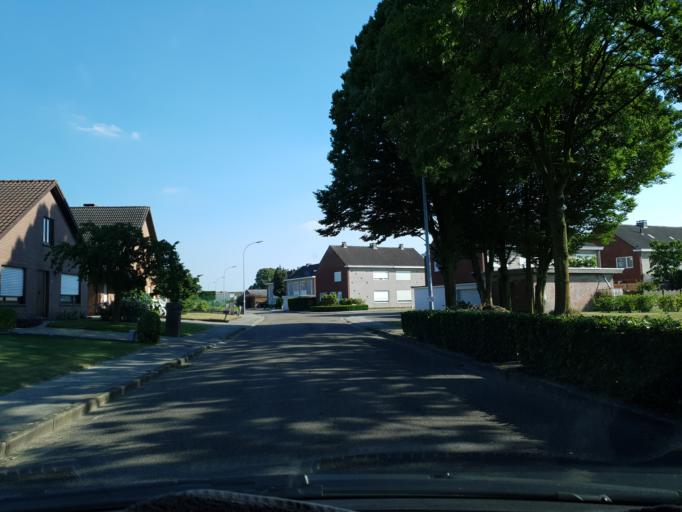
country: BE
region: Flanders
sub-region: Provincie Antwerpen
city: Merksplas
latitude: 51.3596
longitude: 4.8676
